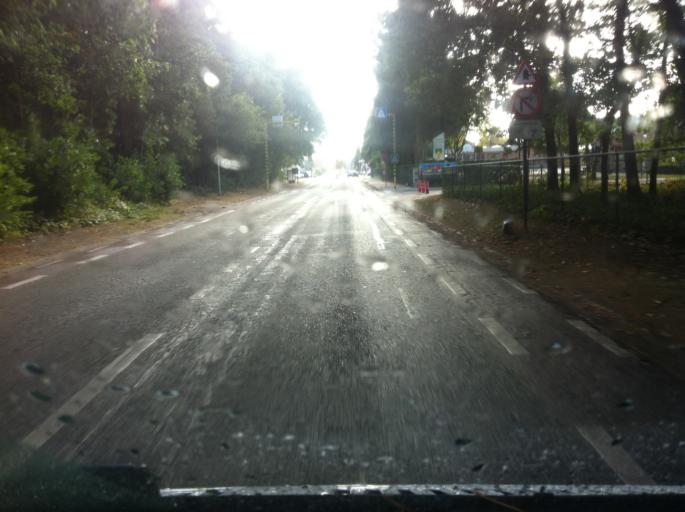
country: BE
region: Flanders
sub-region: Provincie Limburg
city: Maasmechelen
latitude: 50.9712
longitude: 5.6806
